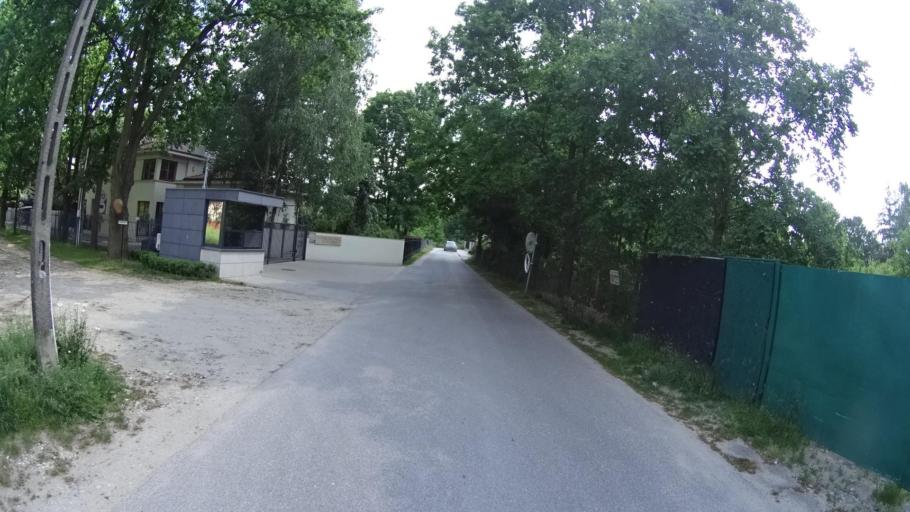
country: PL
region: Masovian Voivodeship
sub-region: Powiat piaseczynski
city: Konstancin-Jeziorna
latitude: 52.1001
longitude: 21.1058
